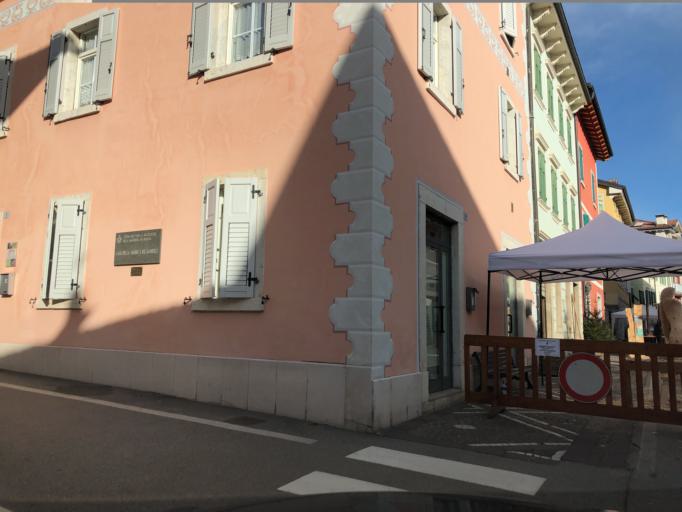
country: IT
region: Trentino-Alto Adige
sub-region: Provincia di Trento
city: Brentonico
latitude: 45.8172
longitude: 10.9543
